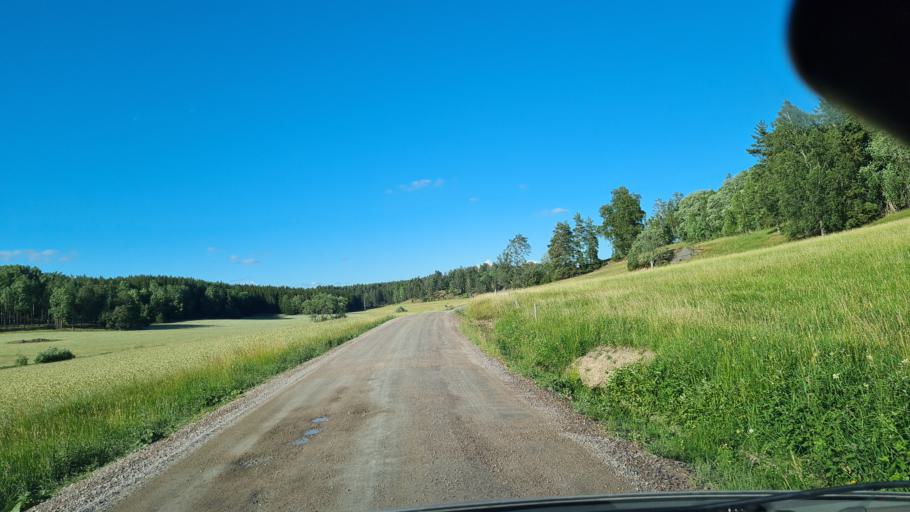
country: SE
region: Soedermanland
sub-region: Nykopings Kommun
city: Nykoping
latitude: 58.9220
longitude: 17.0479
